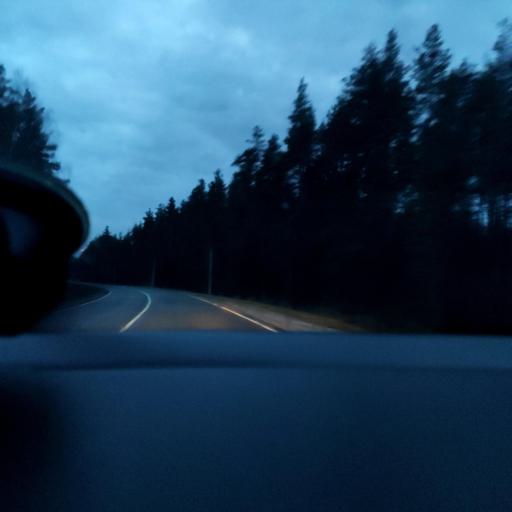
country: RU
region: Moskovskaya
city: Shaturtorf
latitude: 55.4476
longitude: 39.4357
